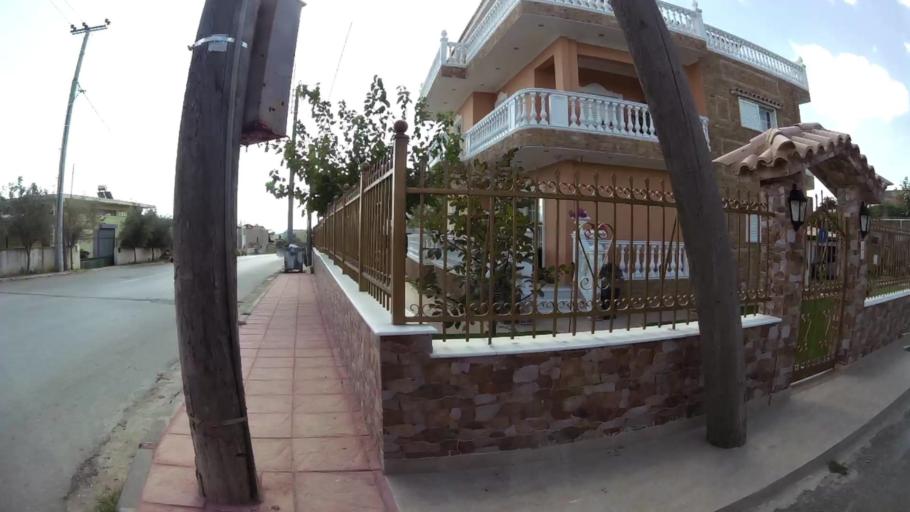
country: GR
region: Attica
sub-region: Nomarchia Anatolikis Attikis
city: Acharnes
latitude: 38.1030
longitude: 23.7501
